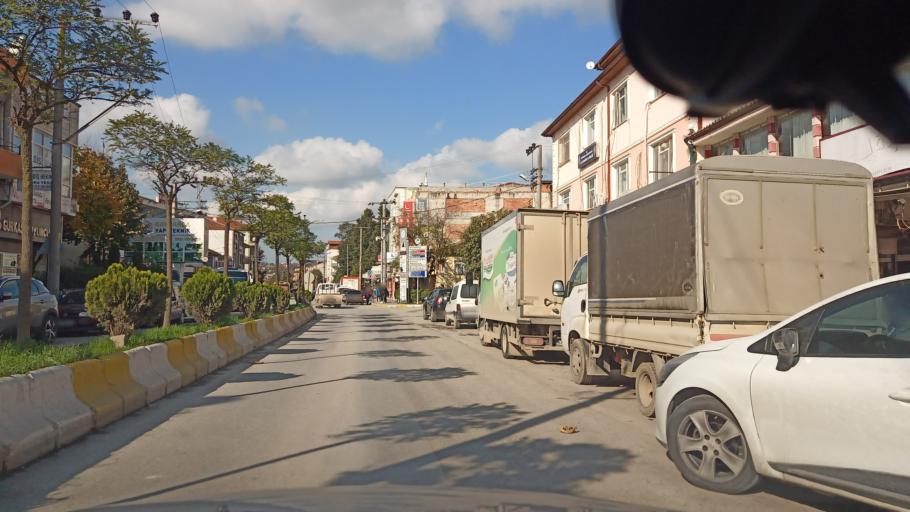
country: TR
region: Sakarya
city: Kaynarca
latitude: 41.0336
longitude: 30.3061
